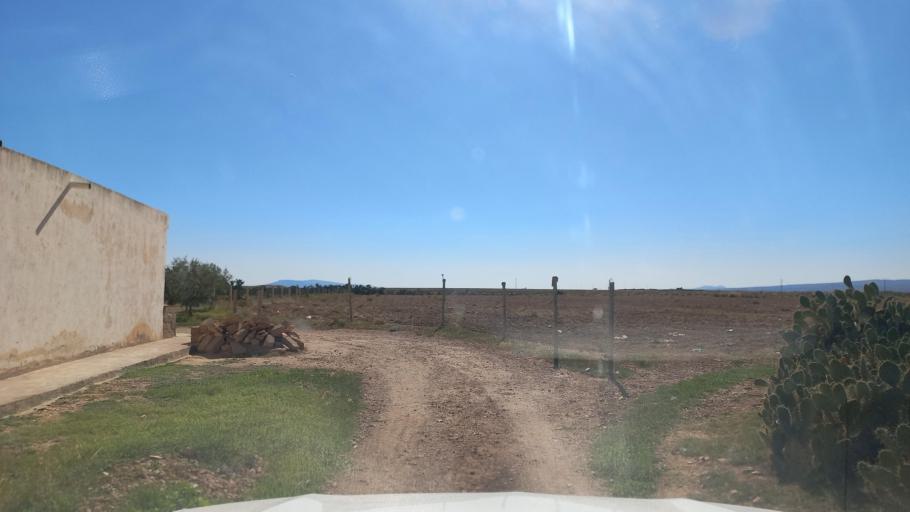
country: TN
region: Al Qasrayn
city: Sbiba
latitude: 35.3957
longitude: 9.1176
